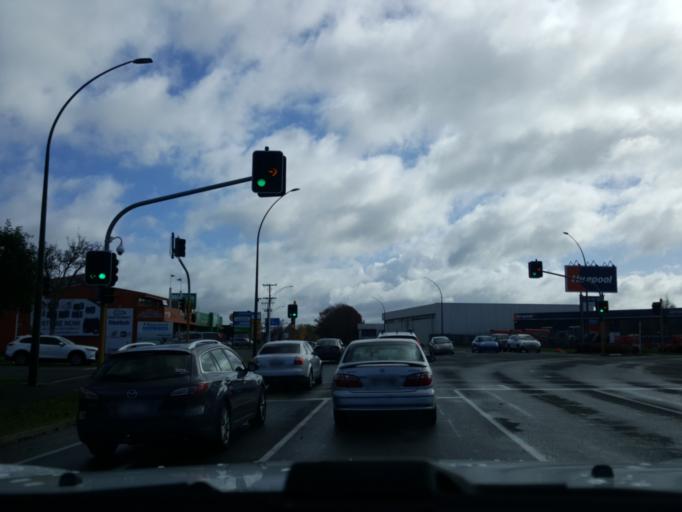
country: NZ
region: Waikato
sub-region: Hamilton City
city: Hamilton
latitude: -37.7524
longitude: 175.2405
